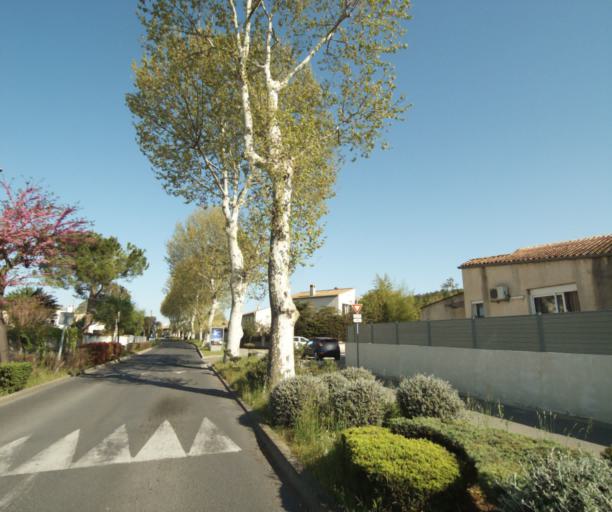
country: FR
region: Languedoc-Roussillon
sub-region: Departement de l'Herault
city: Jacou
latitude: 43.6593
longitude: 3.9088
